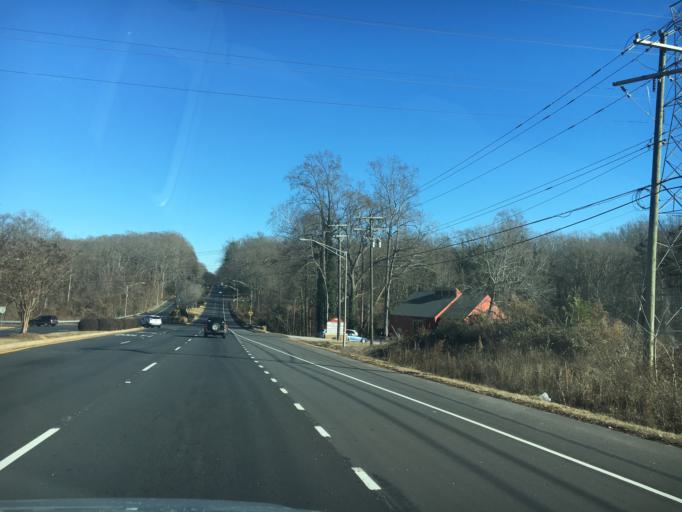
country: US
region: South Carolina
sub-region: Spartanburg County
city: Saxon
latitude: 34.9380
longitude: -81.9738
